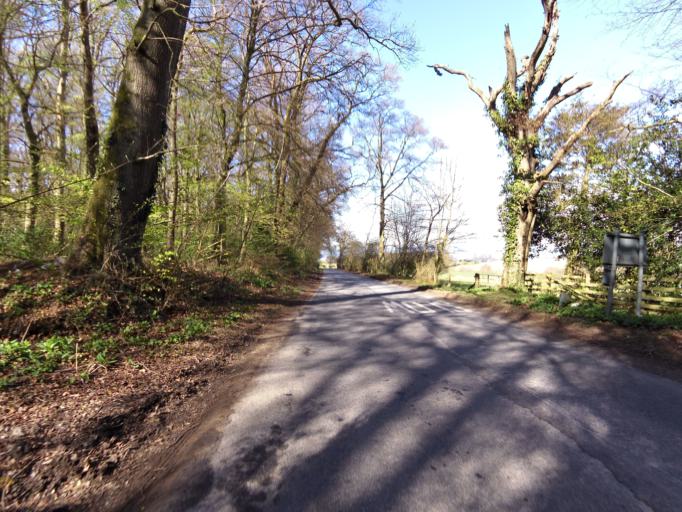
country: GB
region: Scotland
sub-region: Dundee City
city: Dundee
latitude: 56.4087
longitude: -3.0266
